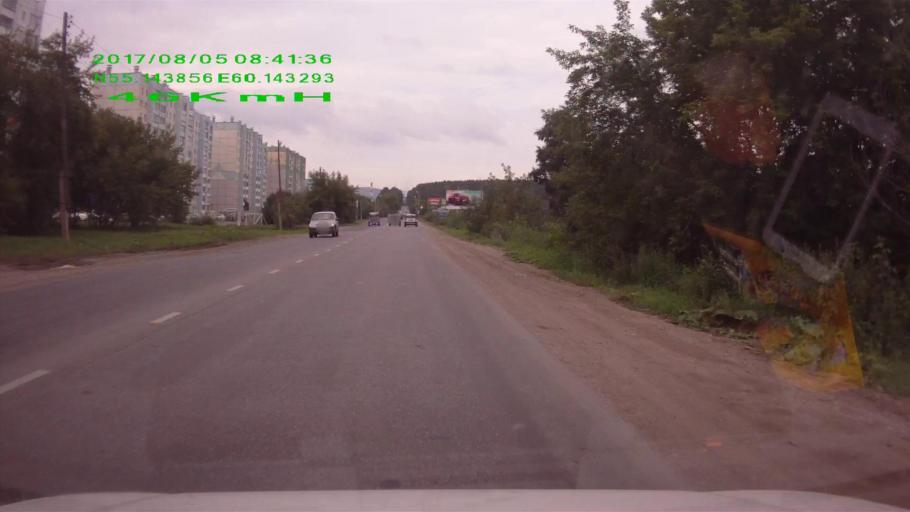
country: RU
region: Chelyabinsk
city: Turgoyak
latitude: 55.1436
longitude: 60.1433
